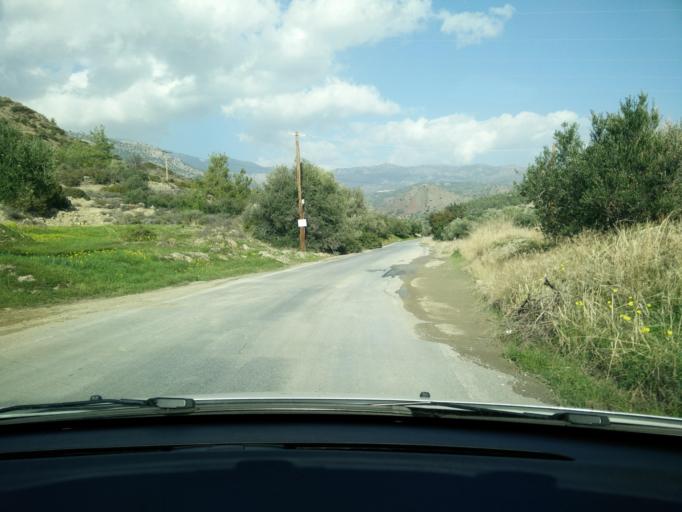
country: GR
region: Crete
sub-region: Nomos Lasithiou
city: Gra Liyia
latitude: 35.0187
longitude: 25.5837
